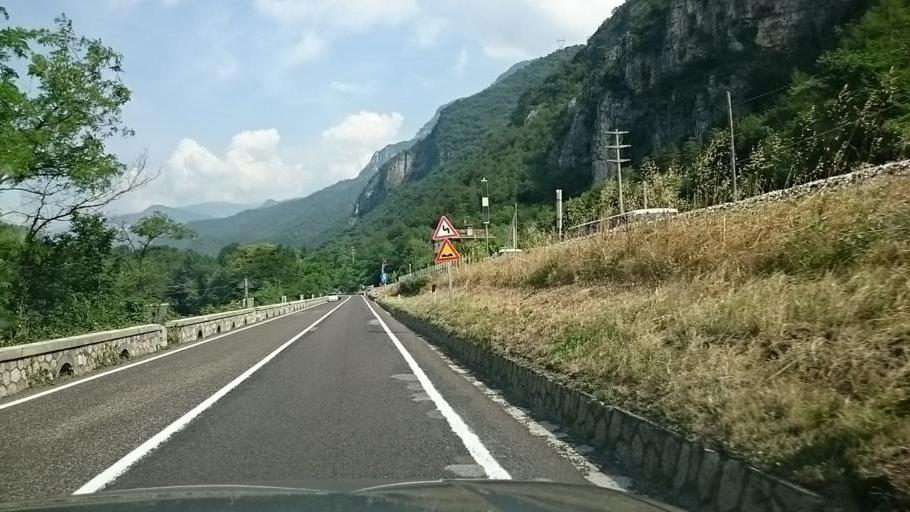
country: IT
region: Veneto
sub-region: Provincia di Vicenza
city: Campolongo sul Brenta
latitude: 45.8290
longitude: 11.7037
